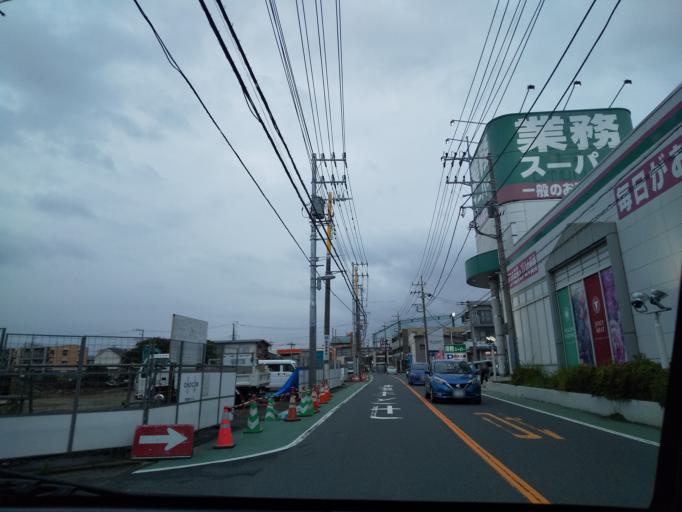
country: JP
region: Kanagawa
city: Fujisawa
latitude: 35.4080
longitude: 139.5007
